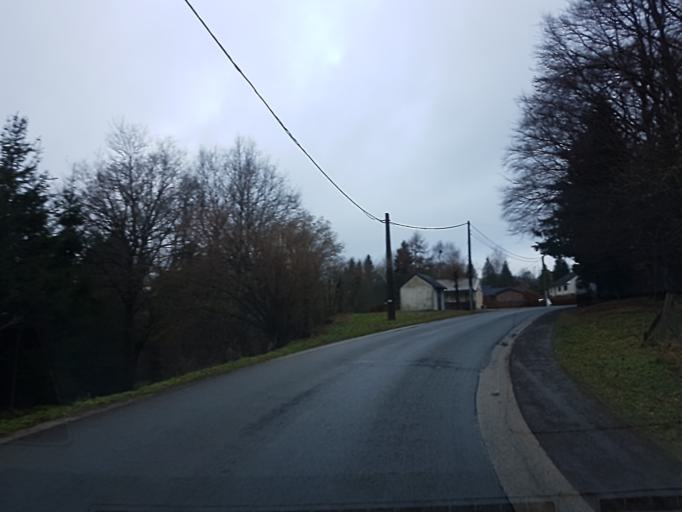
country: BE
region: Wallonia
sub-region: Province de Liege
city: Waimes
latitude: 50.4676
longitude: 6.0862
